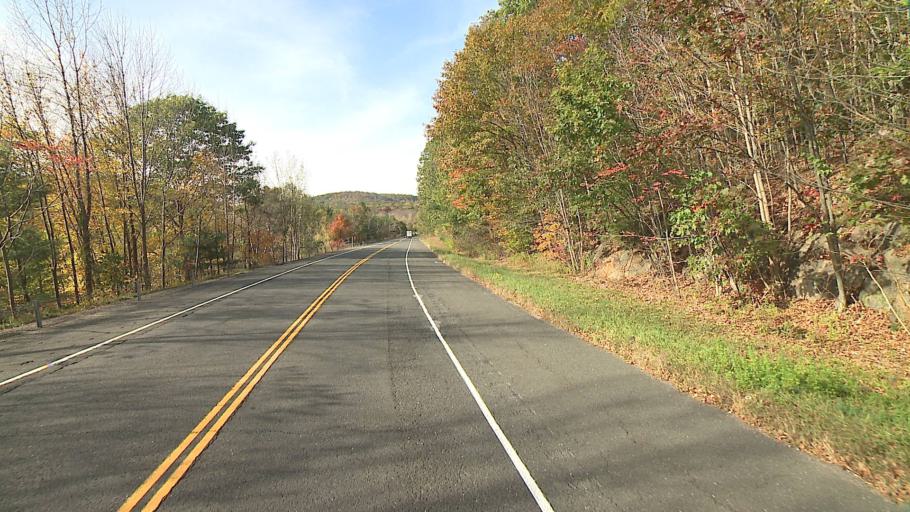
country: US
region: Connecticut
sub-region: Litchfield County
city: Winchester Center
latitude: 41.9408
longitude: -73.1086
